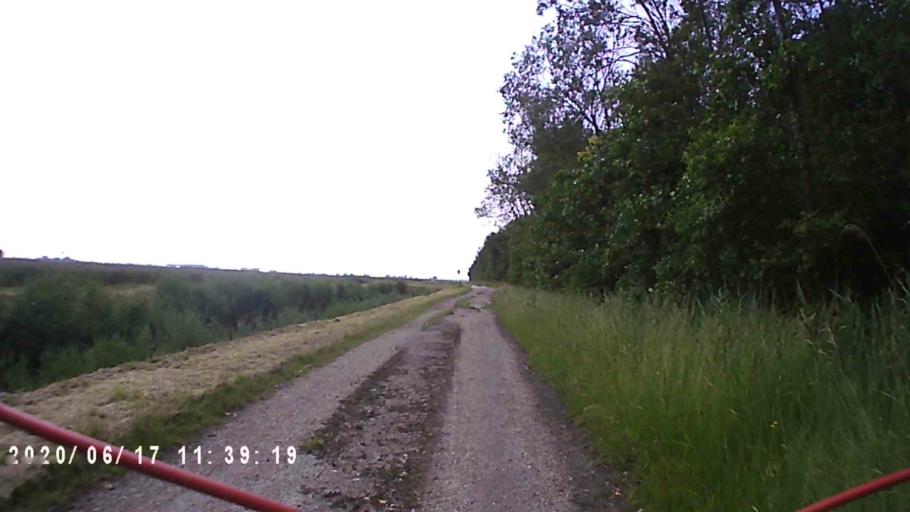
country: NL
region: Groningen
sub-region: Gemeente De Marne
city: Ulrum
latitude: 53.3621
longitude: 6.2725
